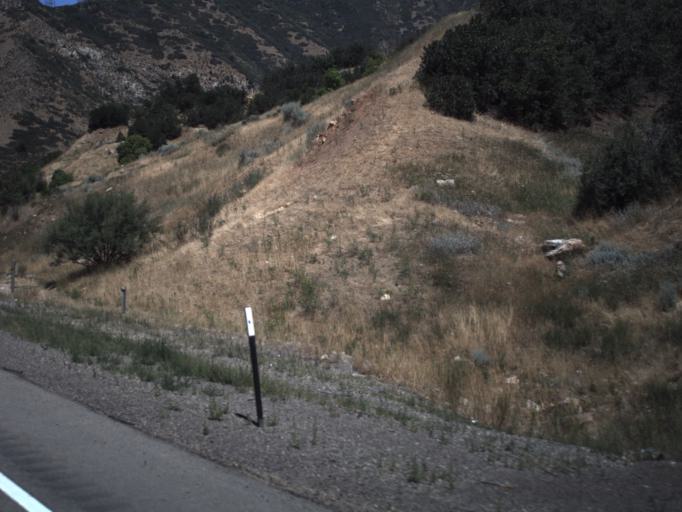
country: US
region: Utah
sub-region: Utah County
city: Mapleton
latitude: 40.0305
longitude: -111.5114
